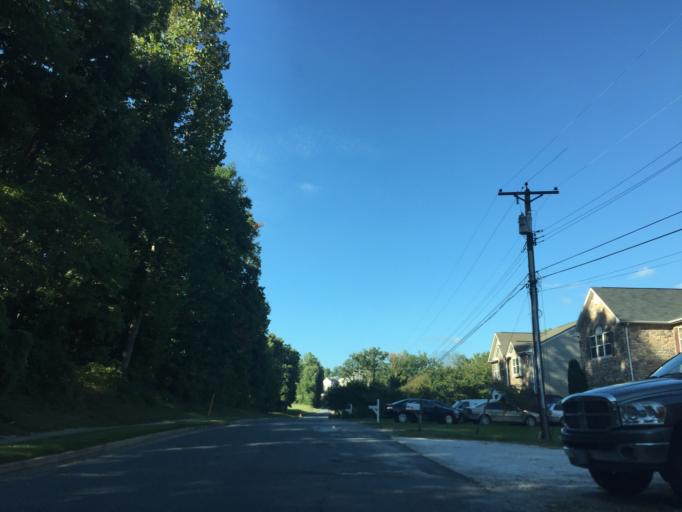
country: US
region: Maryland
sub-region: Baltimore County
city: Rossville
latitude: 39.3555
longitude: -76.4971
